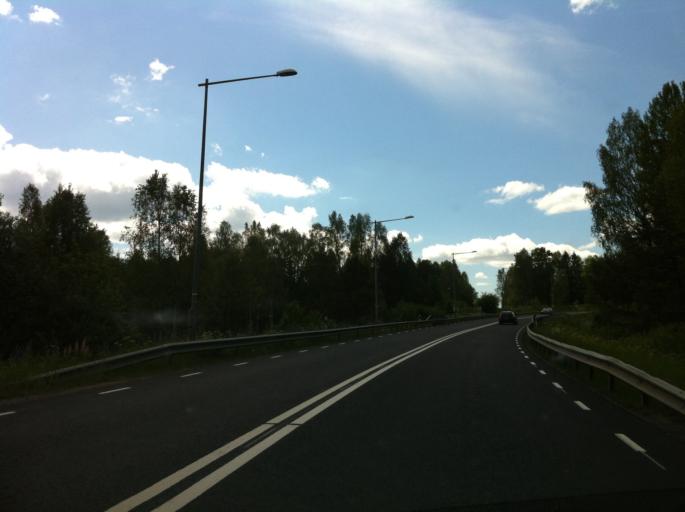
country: SE
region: Vaestra Goetaland
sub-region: Amals Kommun
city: Amal
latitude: 59.0756
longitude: 12.7006
